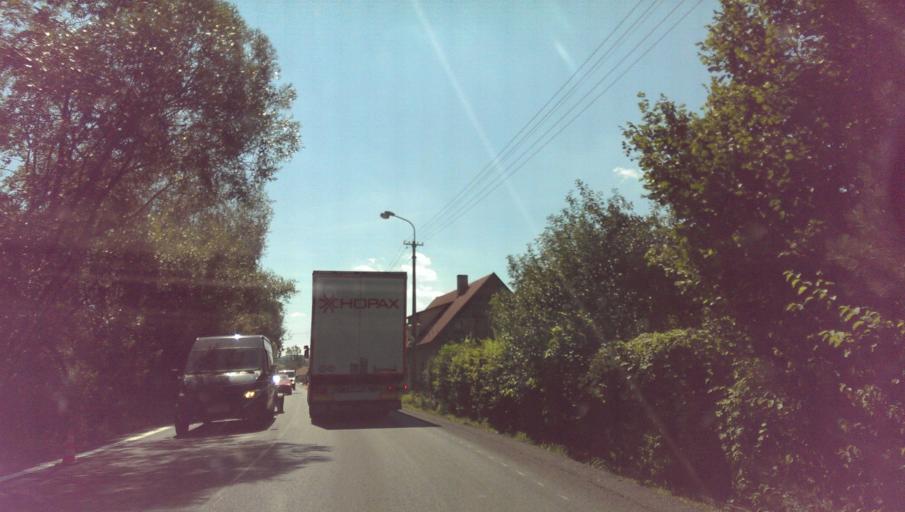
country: CZ
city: Lichnov (o. Novy Jicin)
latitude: 49.5888
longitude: 18.1907
